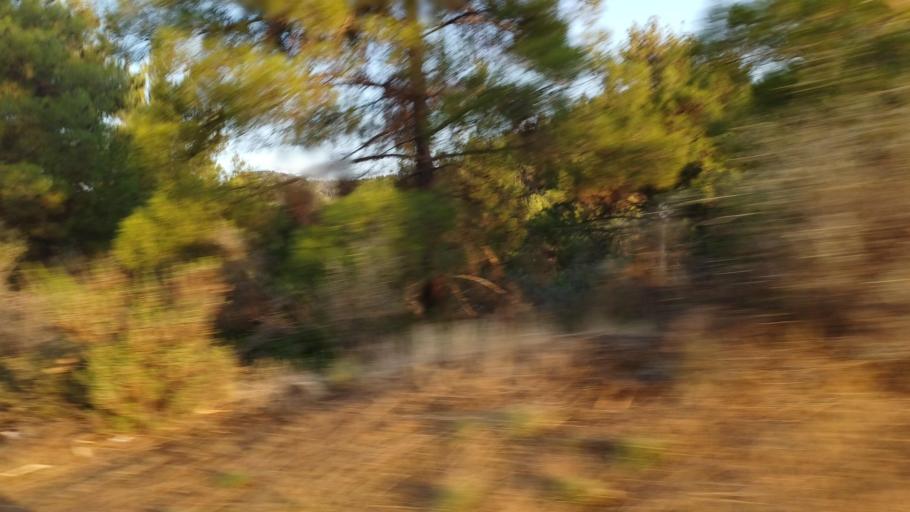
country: CY
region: Lefkosia
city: Lythrodontas
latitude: 34.9462
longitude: 33.2817
